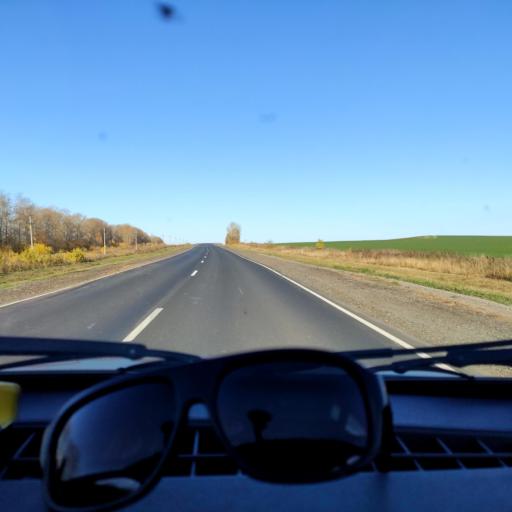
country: RU
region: Bashkortostan
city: Blagoveshchensk
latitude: 55.0691
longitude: 55.9121
